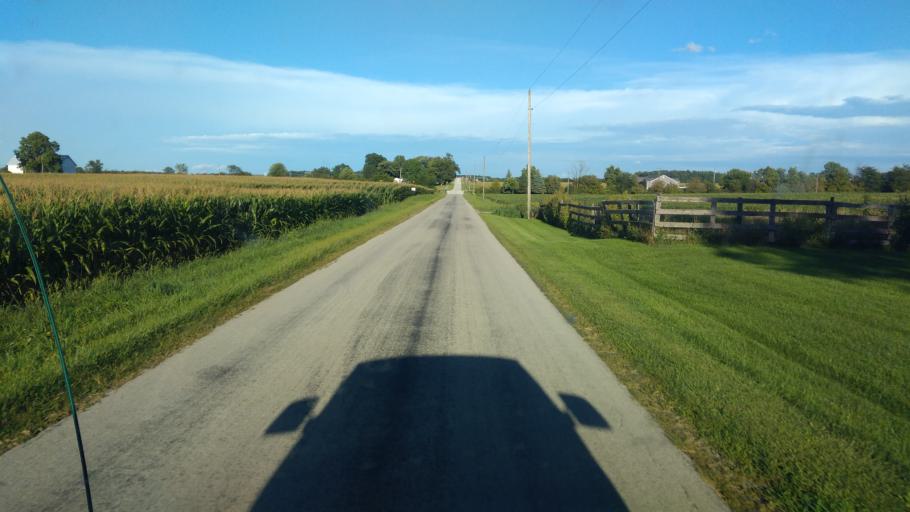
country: US
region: Ohio
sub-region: Wyandot County
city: Upper Sandusky
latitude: 40.8470
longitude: -83.3387
